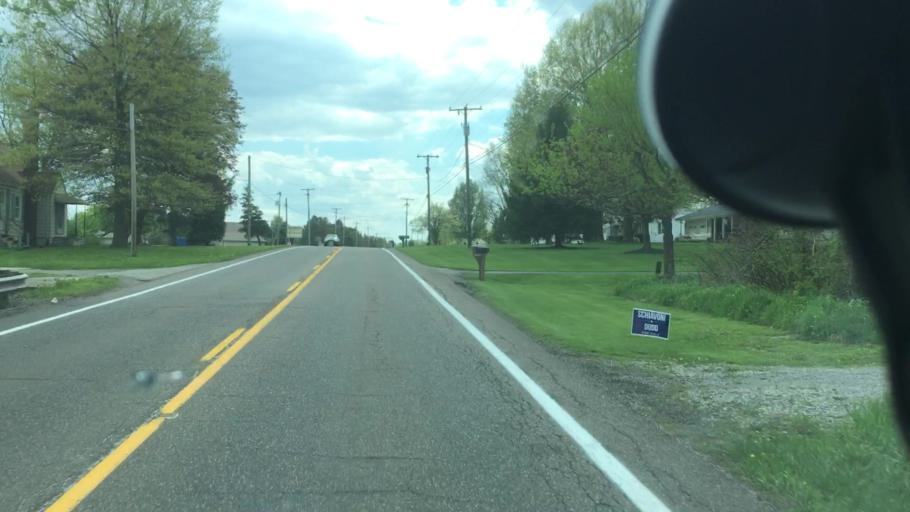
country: US
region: Ohio
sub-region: Columbiana County
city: Columbiana
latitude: 40.9098
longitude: -80.6943
